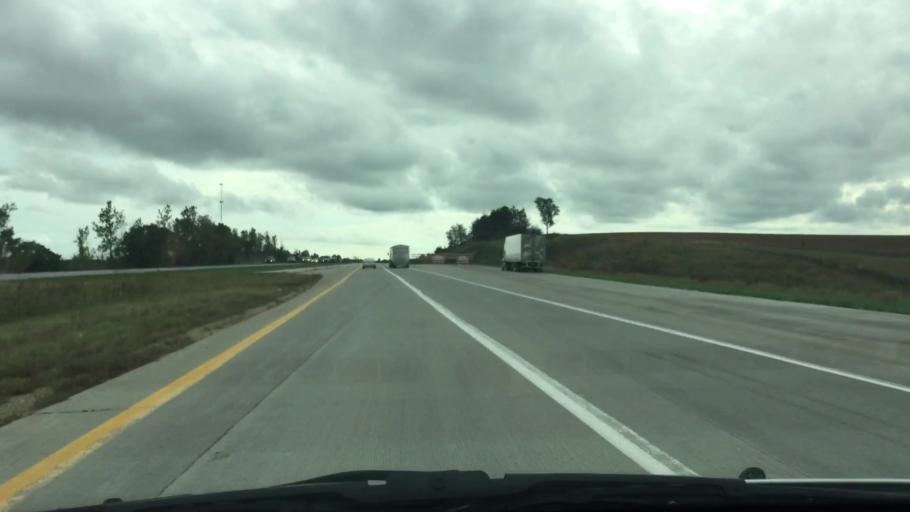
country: US
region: Iowa
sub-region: Warren County
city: Norwalk
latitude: 41.4476
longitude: -93.7801
